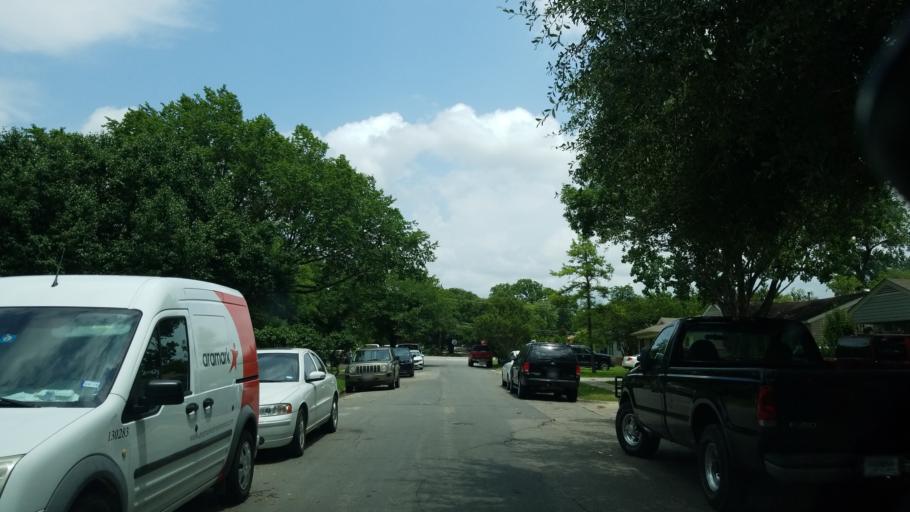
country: US
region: Texas
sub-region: Dallas County
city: Farmers Branch
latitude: 32.8777
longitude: -96.8573
